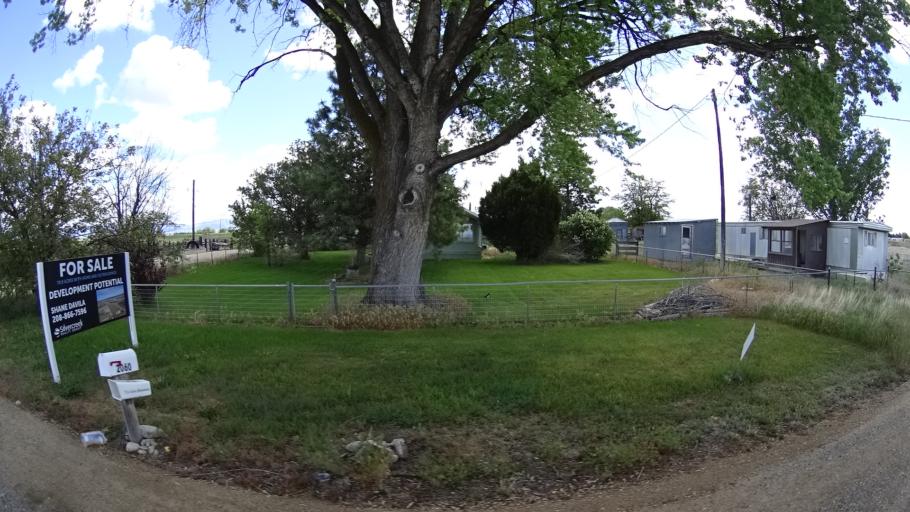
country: US
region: Idaho
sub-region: Ada County
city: Kuna
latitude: 43.5066
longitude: -116.3444
